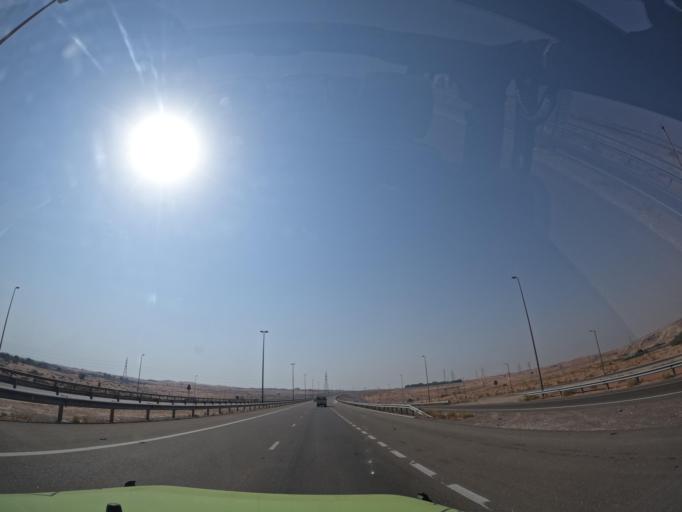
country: OM
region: Al Buraimi
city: Al Buraymi
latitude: 24.3905
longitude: 55.7236
